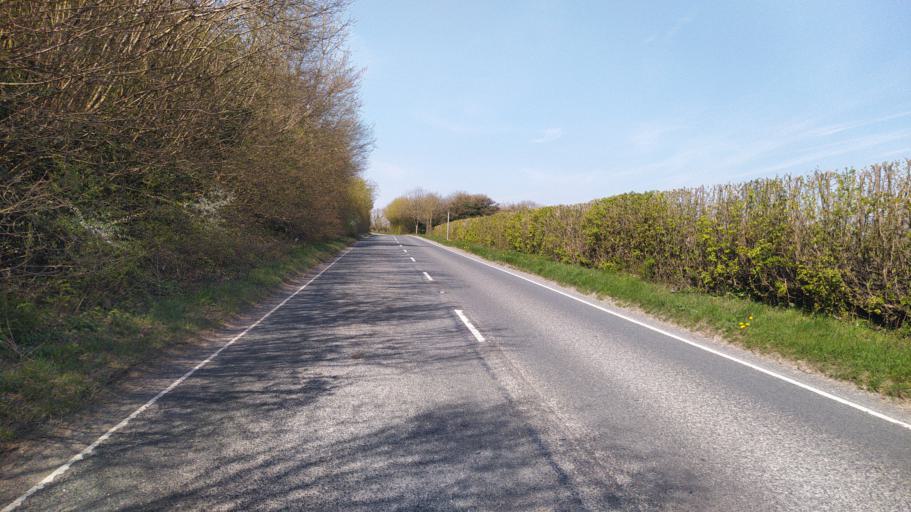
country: GB
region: England
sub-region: Somerset
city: Frome
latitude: 51.2129
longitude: -2.3941
